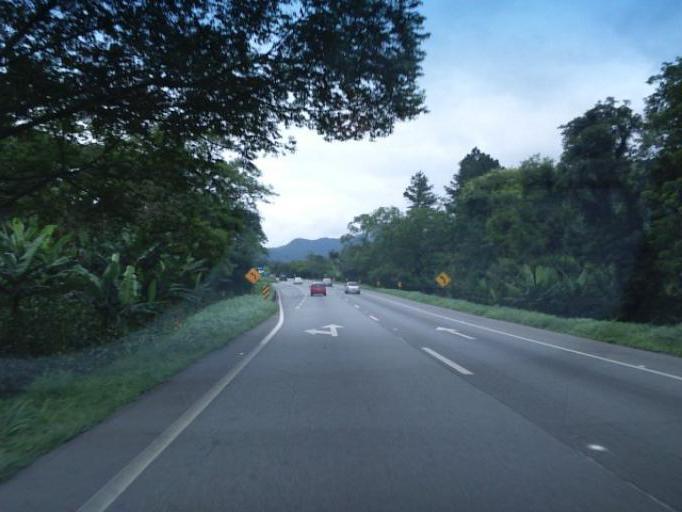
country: BR
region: Parana
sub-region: Guaratuba
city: Guaratuba
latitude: -25.9335
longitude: -48.9100
